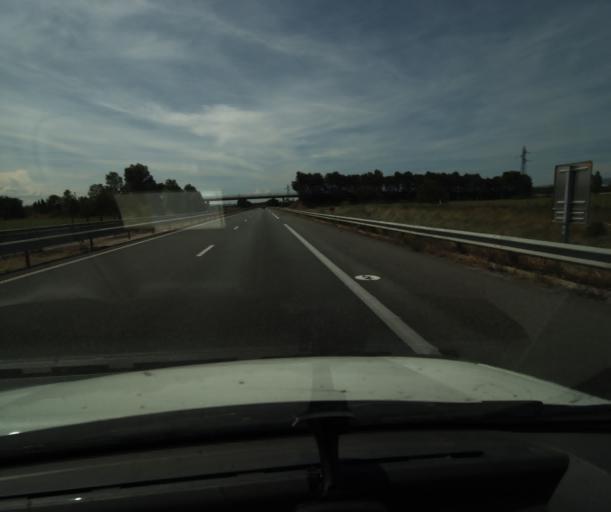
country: FR
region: Languedoc-Roussillon
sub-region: Departement de l'Aude
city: Montreal
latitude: 43.2244
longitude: 2.1628
